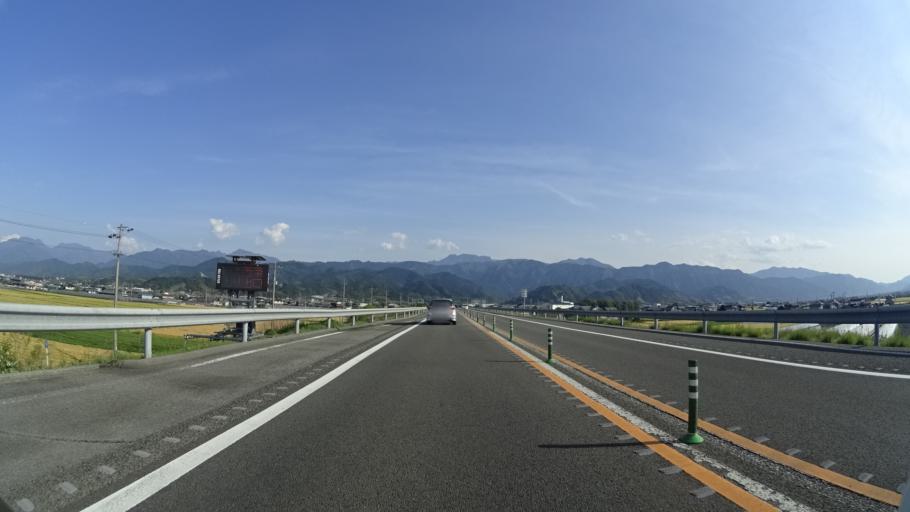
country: JP
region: Ehime
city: Saijo
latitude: 33.9043
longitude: 133.0752
